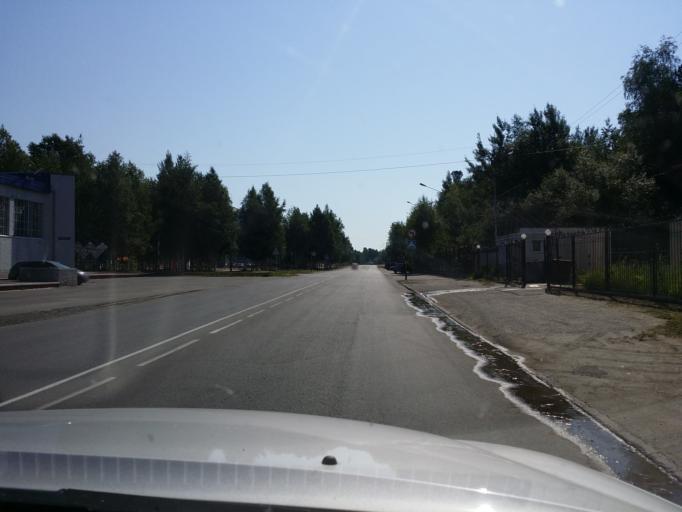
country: RU
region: Tomsk
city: Strezhevoy
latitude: 60.7253
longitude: 77.6004
